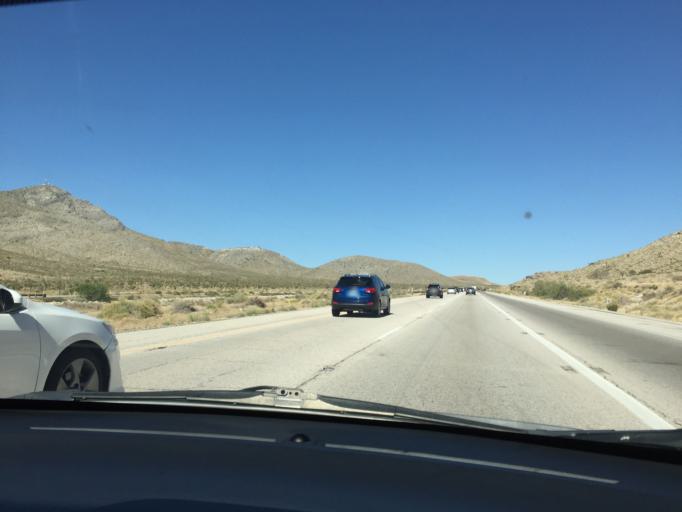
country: US
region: Nevada
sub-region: Clark County
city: Sandy Valley
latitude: 35.4744
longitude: -115.5792
